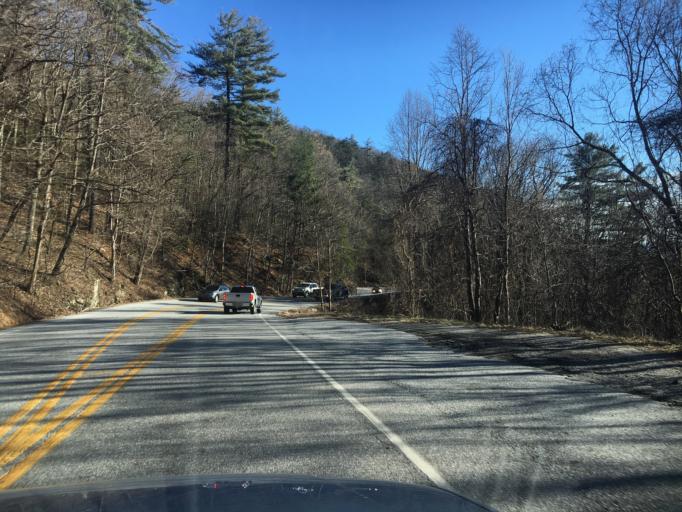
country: US
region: Georgia
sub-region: Union County
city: Blairsville
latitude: 34.7276
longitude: -83.9140
